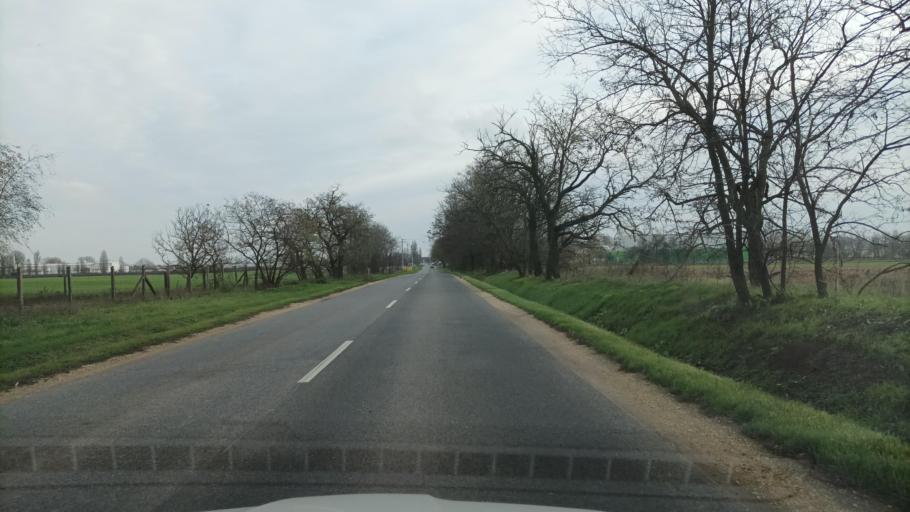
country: HU
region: Pest
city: Ocsa
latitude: 47.3097
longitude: 19.2102
